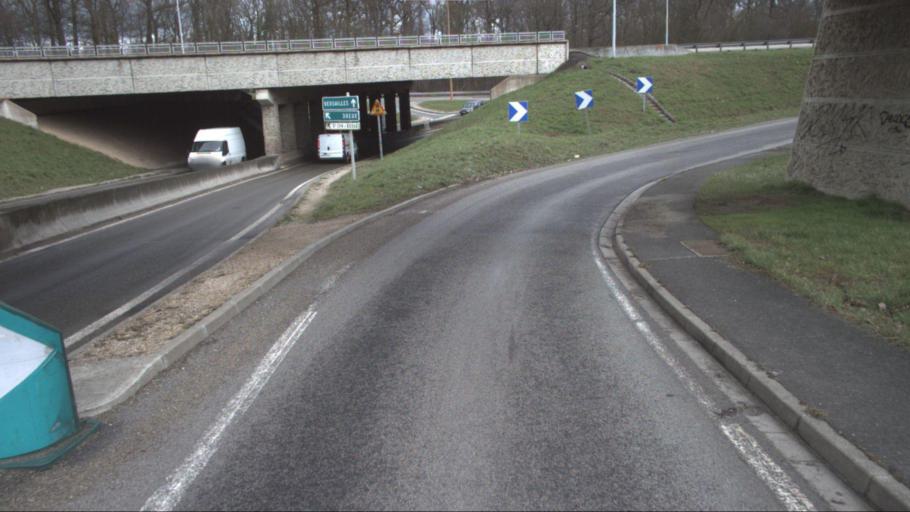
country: FR
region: Ile-de-France
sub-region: Departement des Yvelines
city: Buc
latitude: 48.7904
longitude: 2.1071
